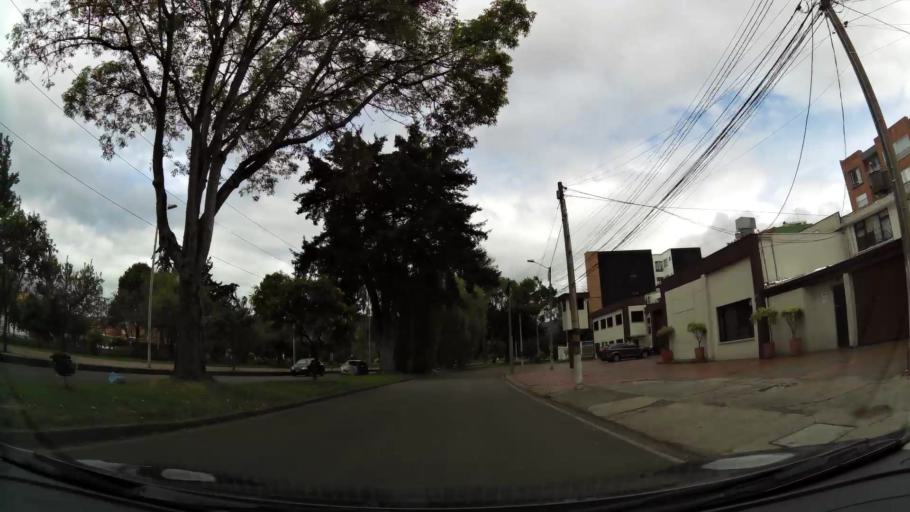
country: CO
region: Bogota D.C.
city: Barrio San Luis
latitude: 4.6971
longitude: -74.0618
